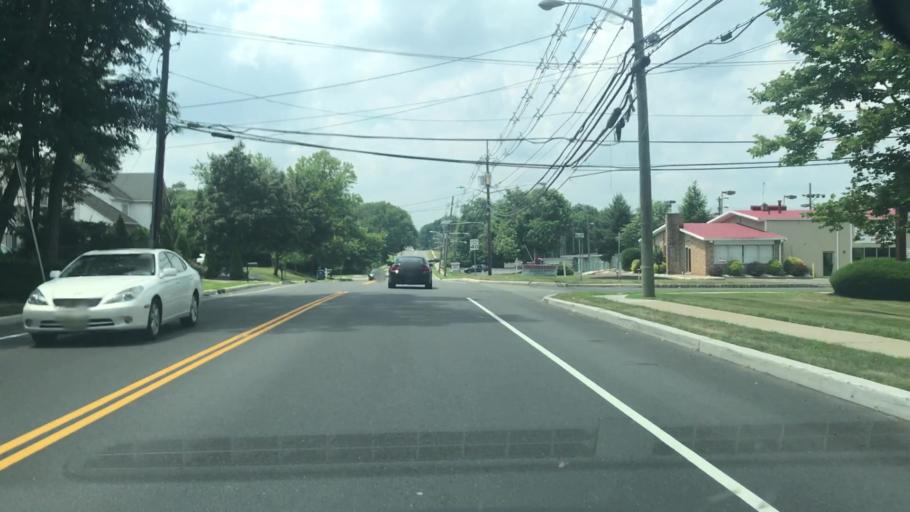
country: US
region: New Jersey
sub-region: Middlesex County
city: Iselin
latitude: 40.5973
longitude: -74.3532
